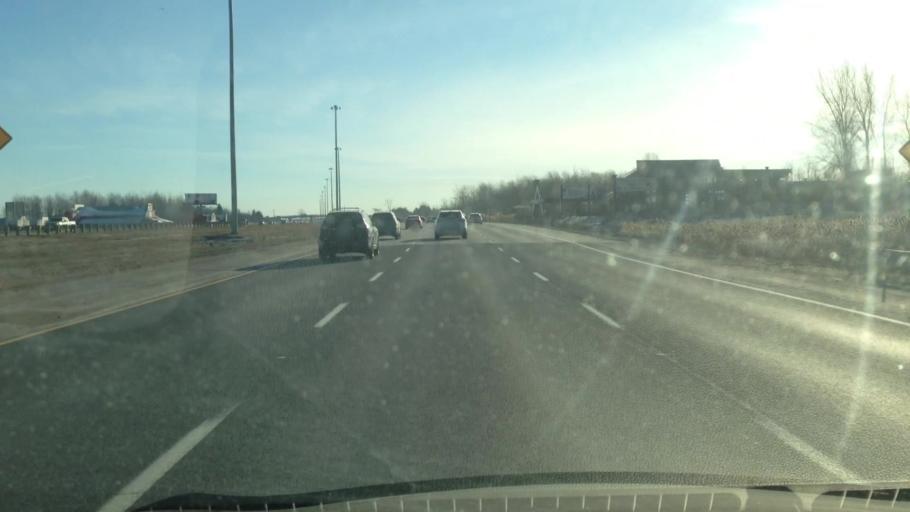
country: CA
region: Quebec
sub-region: Laurentides
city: Saint-Jerome
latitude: 45.7415
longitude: -73.9976
